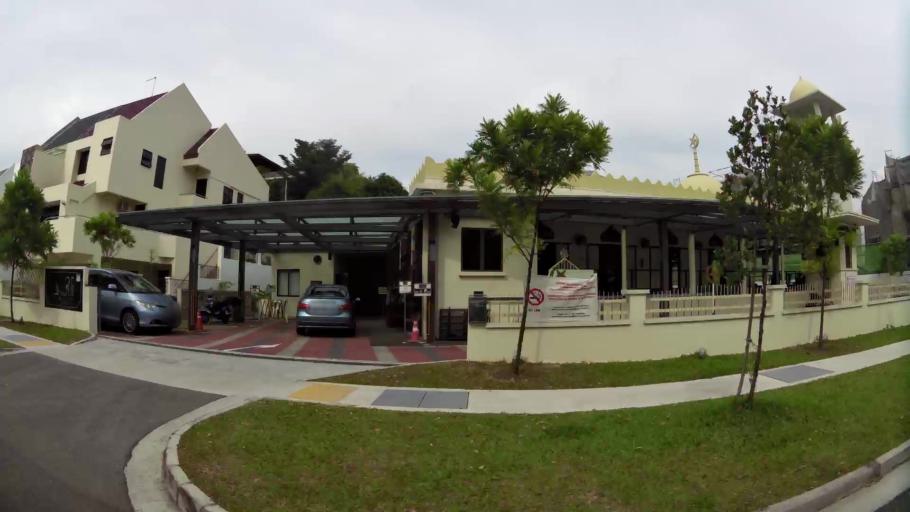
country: SG
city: Singapore
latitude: 1.3232
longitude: 103.7948
